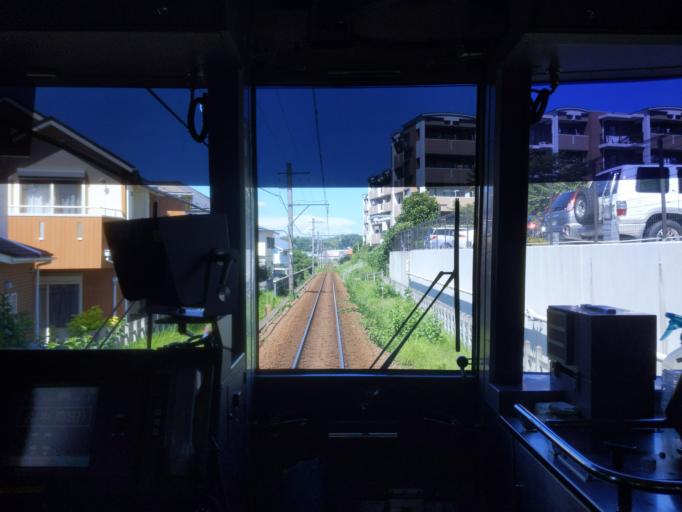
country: JP
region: Tokyo
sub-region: Machida-shi
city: Machida
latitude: 35.5354
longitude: 139.4918
